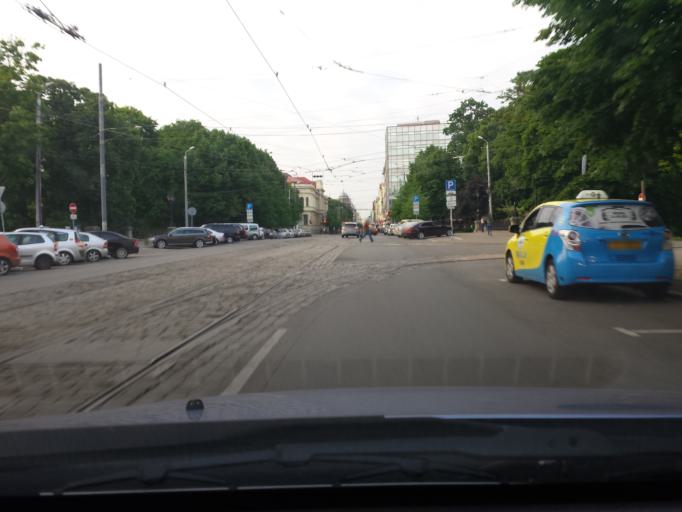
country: LV
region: Riga
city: Riga
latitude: 56.9483
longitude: 24.1153
